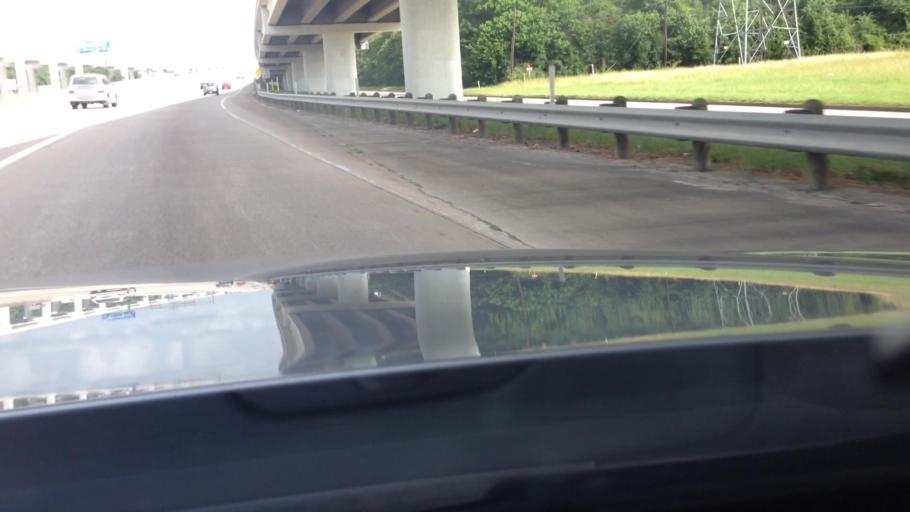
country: US
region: Texas
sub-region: Harris County
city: Hudson
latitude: 29.9411
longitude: -95.5213
